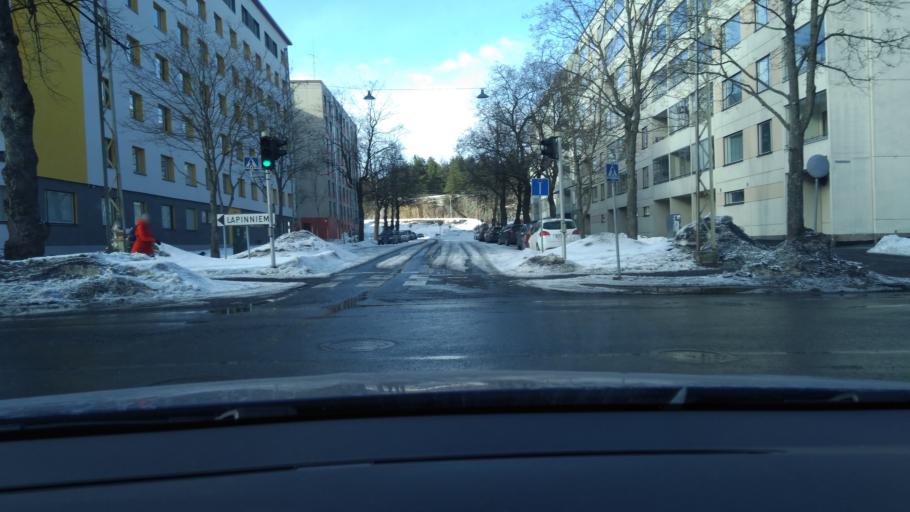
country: FI
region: Pirkanmaa
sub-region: Tampere
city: Tampere
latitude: 61.5054
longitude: 23.7795
